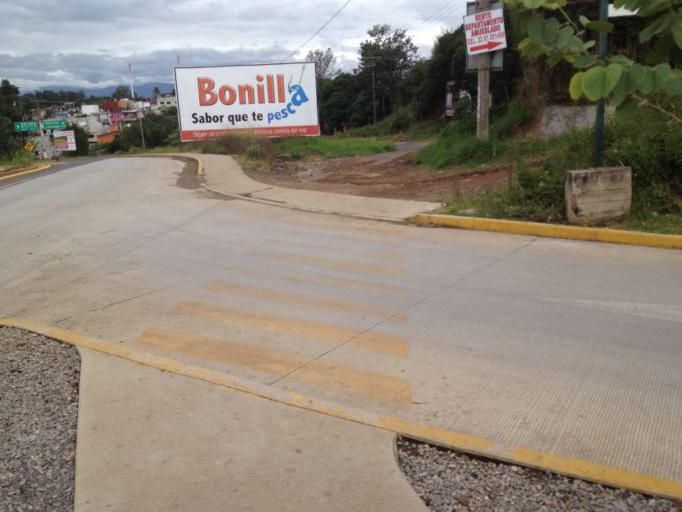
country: MX
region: Veracruz
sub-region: Emiliano Zapata
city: Las Trancas
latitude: 19.5025
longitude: -96.8605
